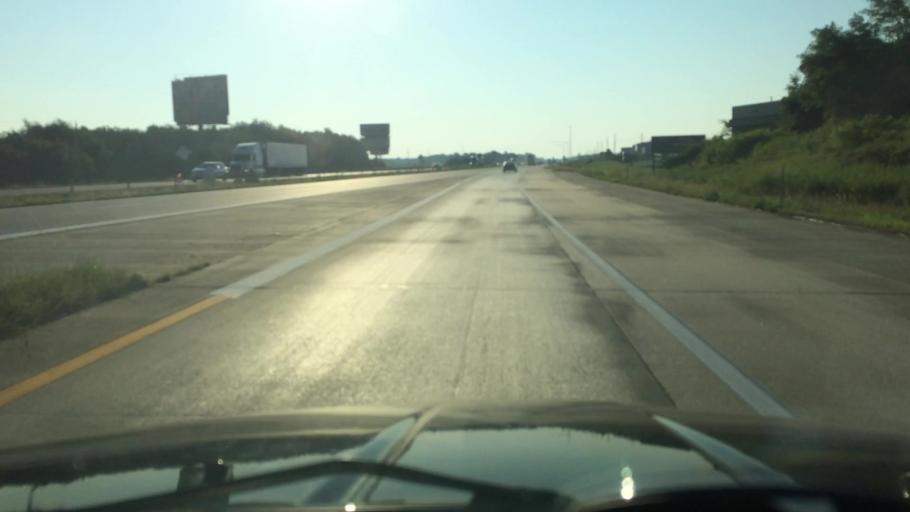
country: US
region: Missouri
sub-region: Greene County
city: Springfield
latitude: 37.2500
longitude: -93.2184
